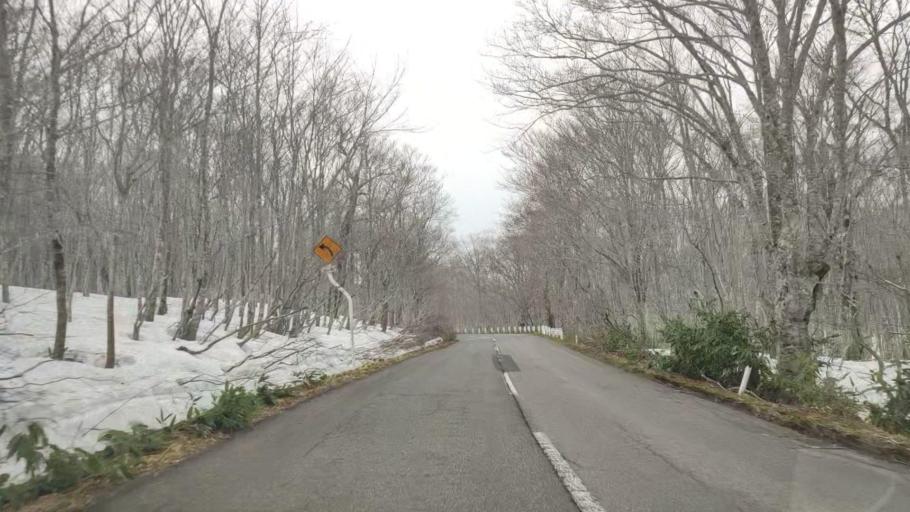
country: JP
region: Aomori
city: Aomori Shi
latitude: 40.6494
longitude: 140.9454
